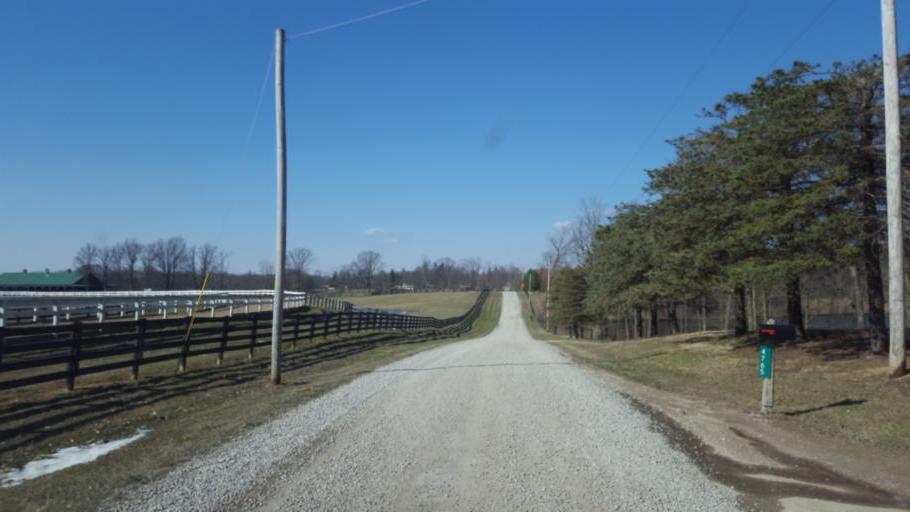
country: US
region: Ohio
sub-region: Morrow County
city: Mount Gilead
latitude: 40.5314
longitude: -82.7780
